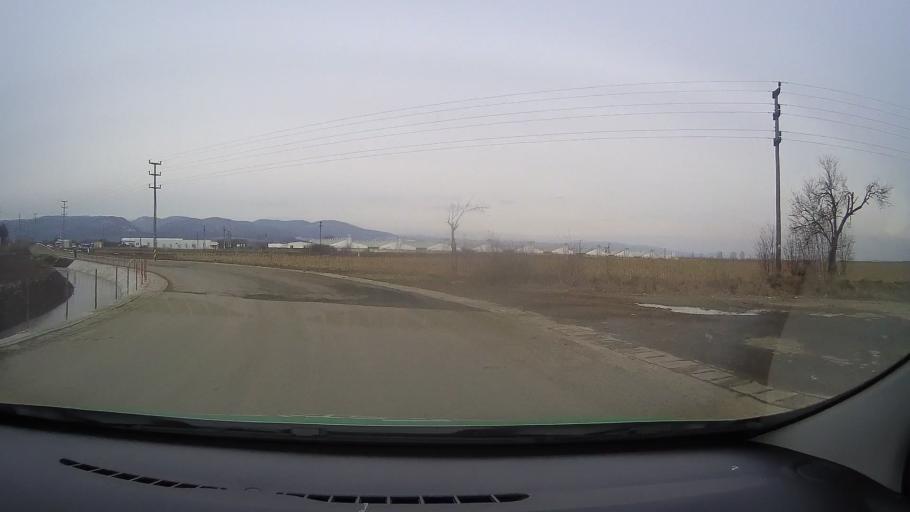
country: RO
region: Hunedoara
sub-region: Comuna Turdas
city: Turdas
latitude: 45.8424
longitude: 23.1376
